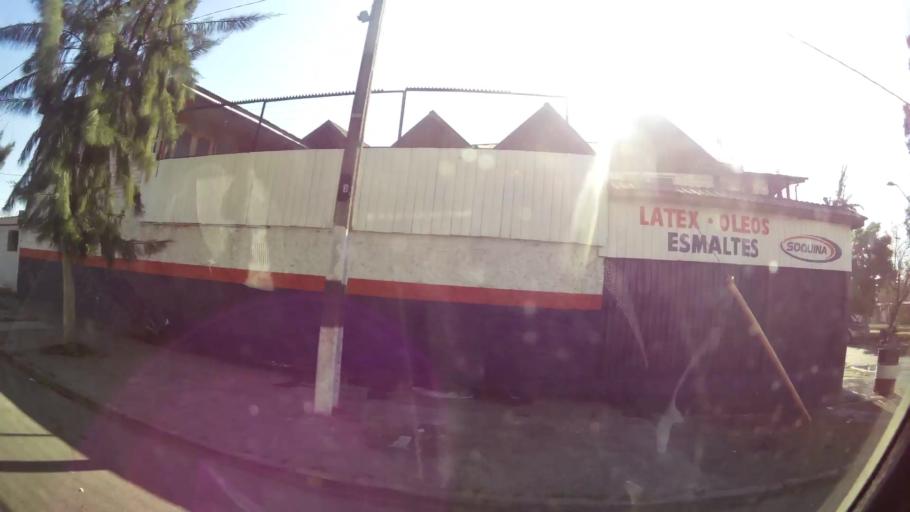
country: CL
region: Santiago Metropolitan
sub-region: Provincia de Santiago
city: Santiago
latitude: -33.5088
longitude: -70.6851
